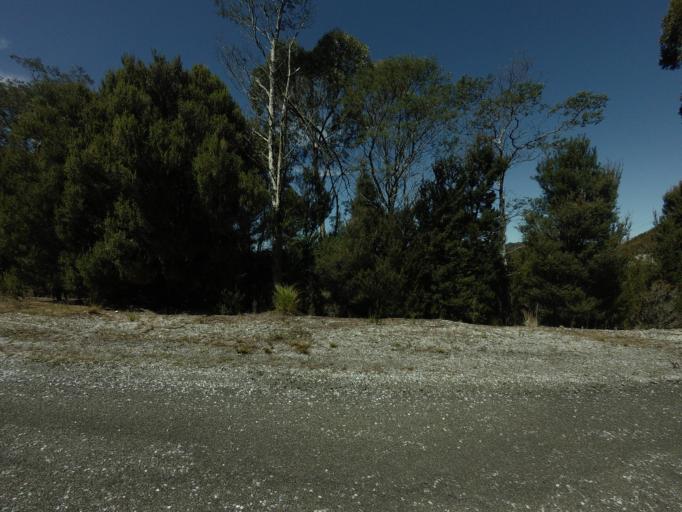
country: AU
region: Tasmania
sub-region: West Coast
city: Queenstown
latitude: -42.7356
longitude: 145.9793
